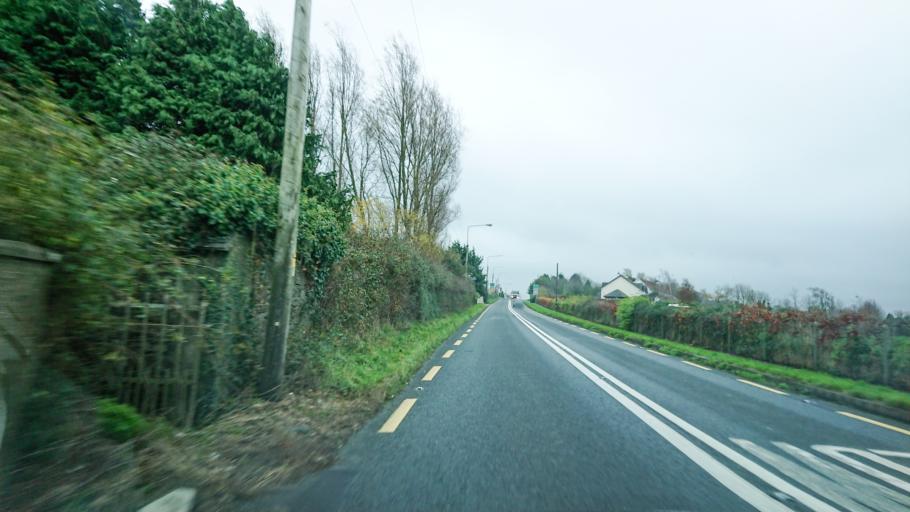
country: IE
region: Leinster
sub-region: Kilkenny
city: Mooncoin
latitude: 52.2984
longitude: -7.2661
